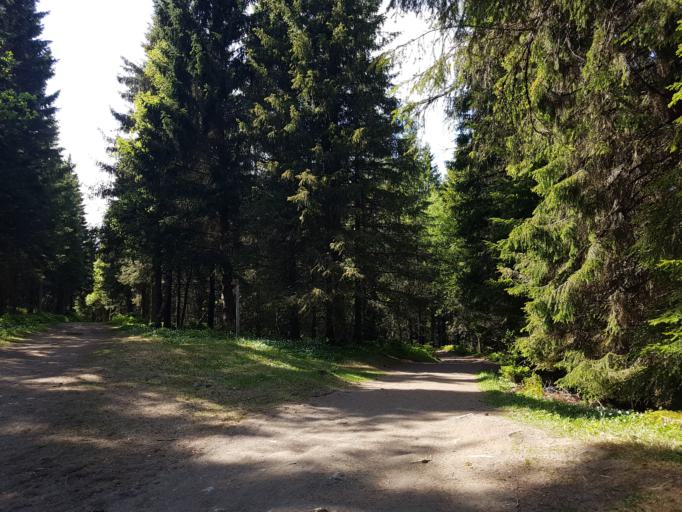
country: NO
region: Sor-Trondelag
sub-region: Trondheim
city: Trondheim
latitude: 63.4175
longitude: 10.3343
